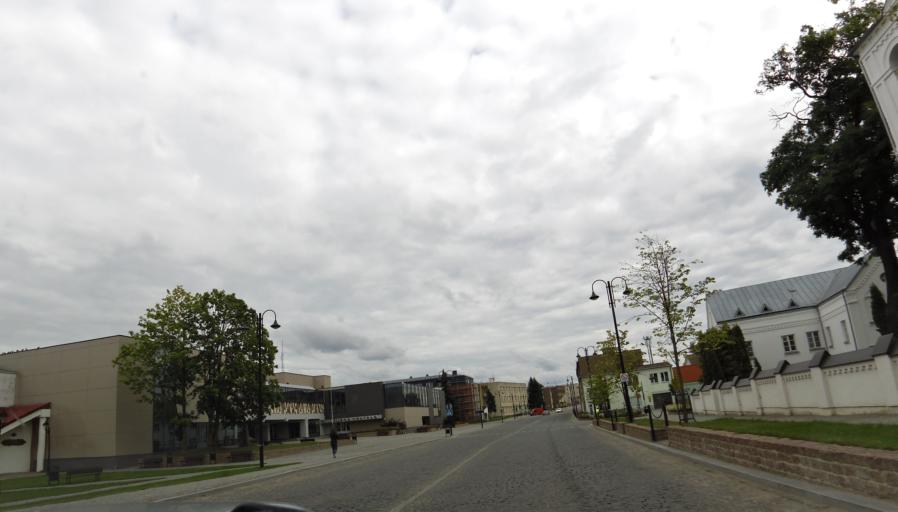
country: LT
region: Panevezys
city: Pasvalys
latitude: 56.0622
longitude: 24.3983
